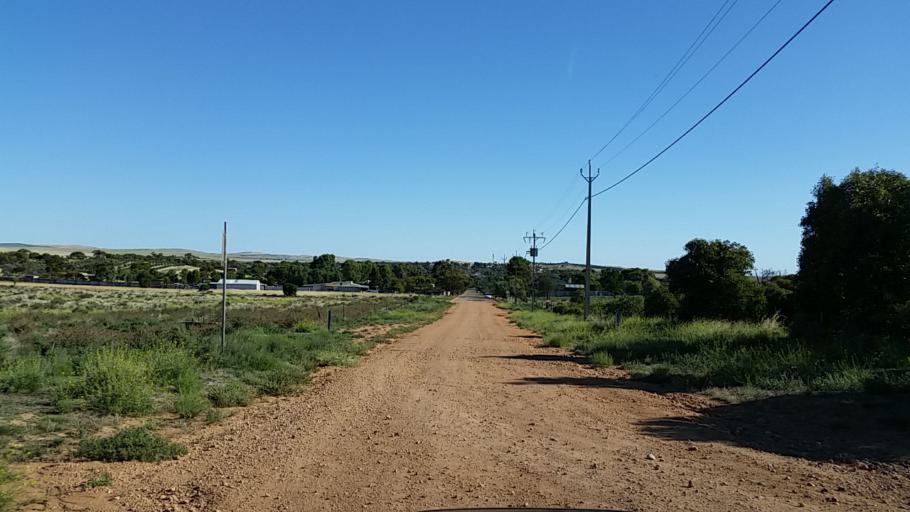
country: AU
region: South Australia
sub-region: Peterborough
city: Peterborough
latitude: -32.9640
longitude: 138.8317
